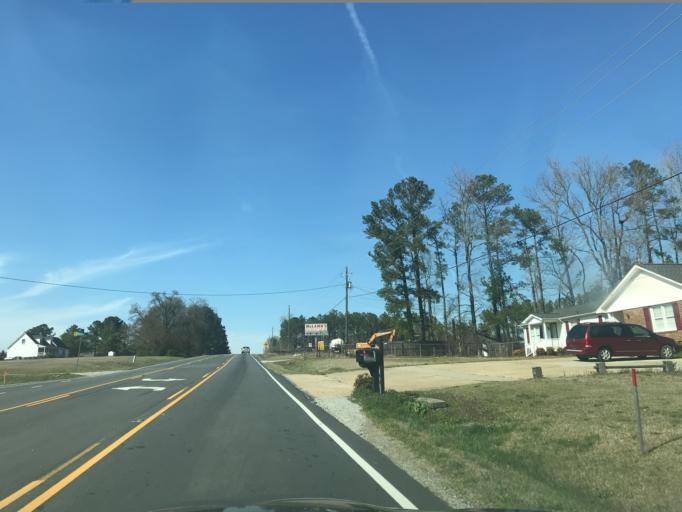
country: US
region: North Carolina
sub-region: Wake County
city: Fuquay-Varina
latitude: 35.5689
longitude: -78.7554
